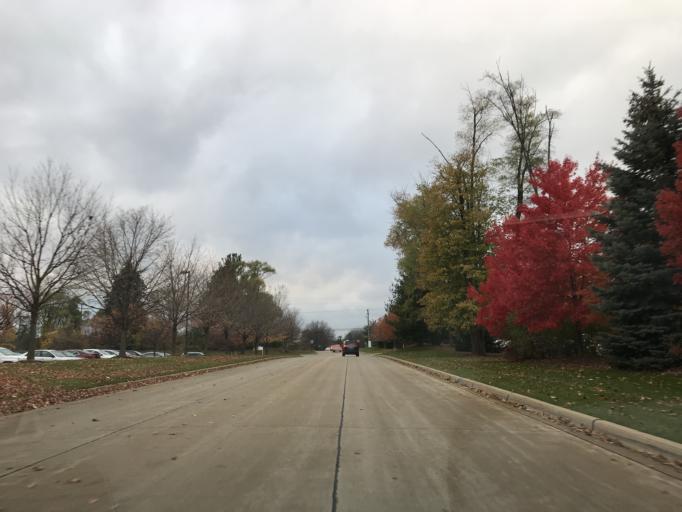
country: US
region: Michigan
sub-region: Oakland County
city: Farmington Hills
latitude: 42.4949
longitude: -83.4145
